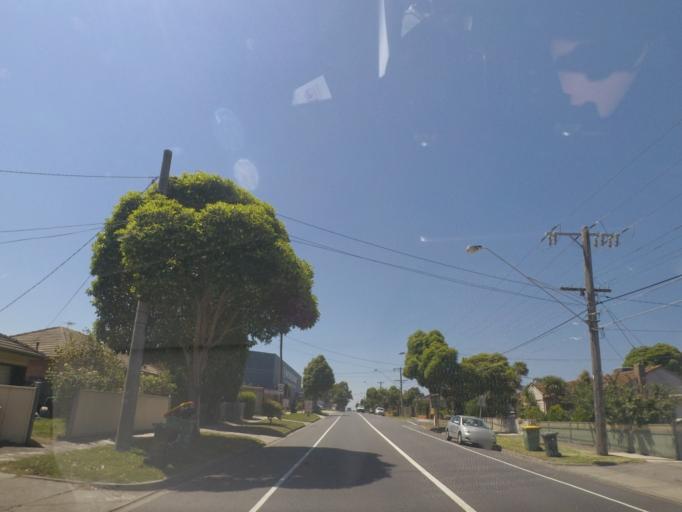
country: AU
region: Victoria
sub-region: Darebin
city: Reservoir
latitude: -37.7117
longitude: 144.9895
